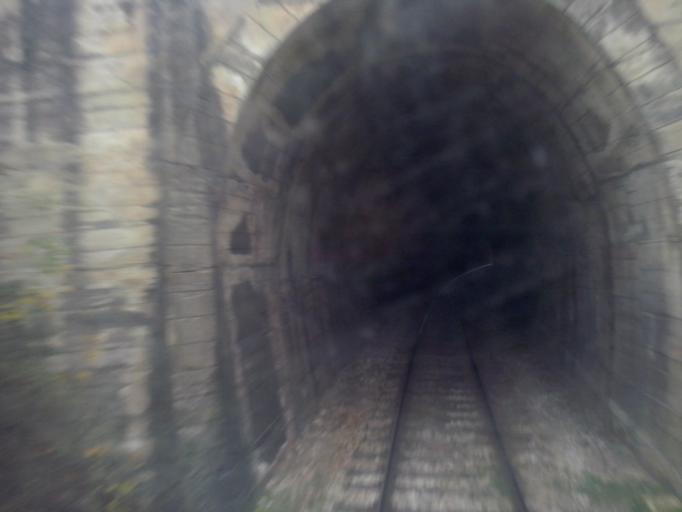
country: RS
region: Central Serbia
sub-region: Zlatiborski Okrug
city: Kosjeric
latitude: 43.9942
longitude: 19.9176
